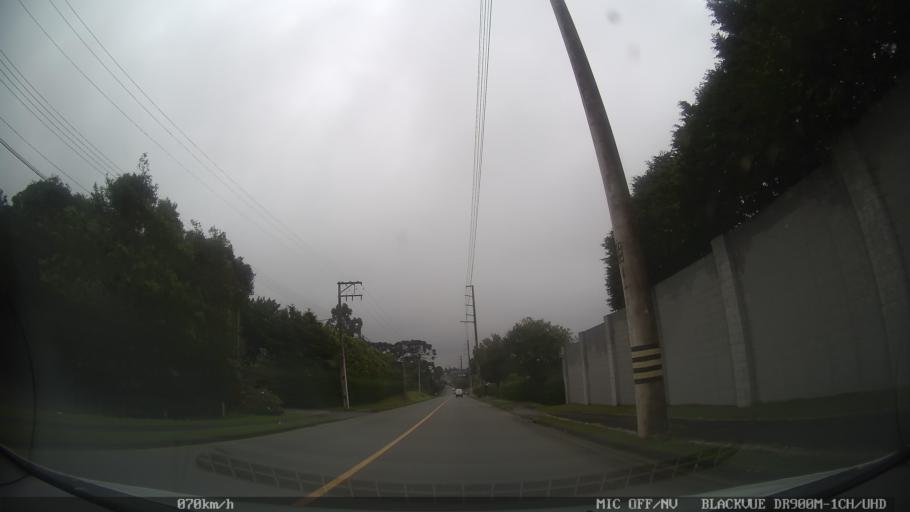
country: BR
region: Parana
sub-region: Sao Jose Dos Pinhais
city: Sao Jose dos Pinhais
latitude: -25.5765
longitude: -49.1704
